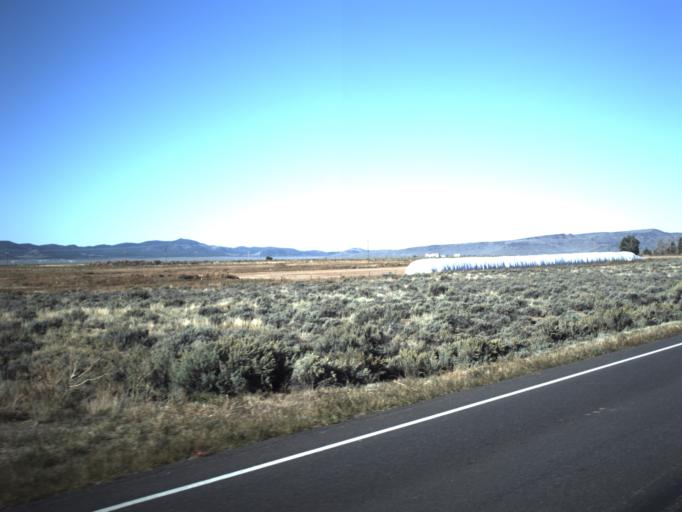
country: US
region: Utah
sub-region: Washington County
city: Enterprise
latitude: 37.7534
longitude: -113.7796
